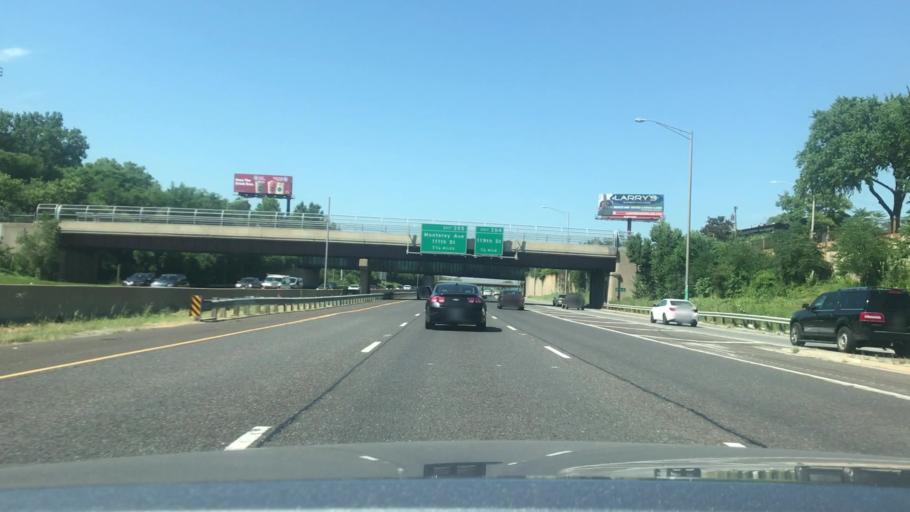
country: US
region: Illinois
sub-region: Cook County
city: Calumet Park
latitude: 41.6657
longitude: -87.6627
